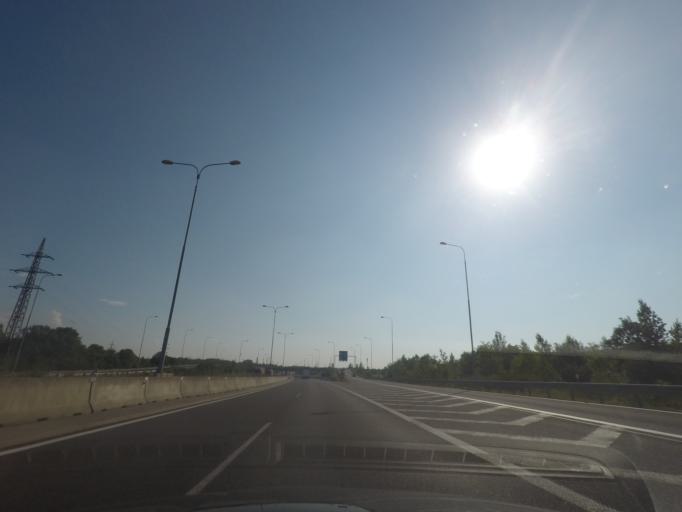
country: CZ
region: Moravskoslezsky
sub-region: Okres Ostrava-Mesto
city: Ostrava
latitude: 49.8600
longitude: 18.2592
